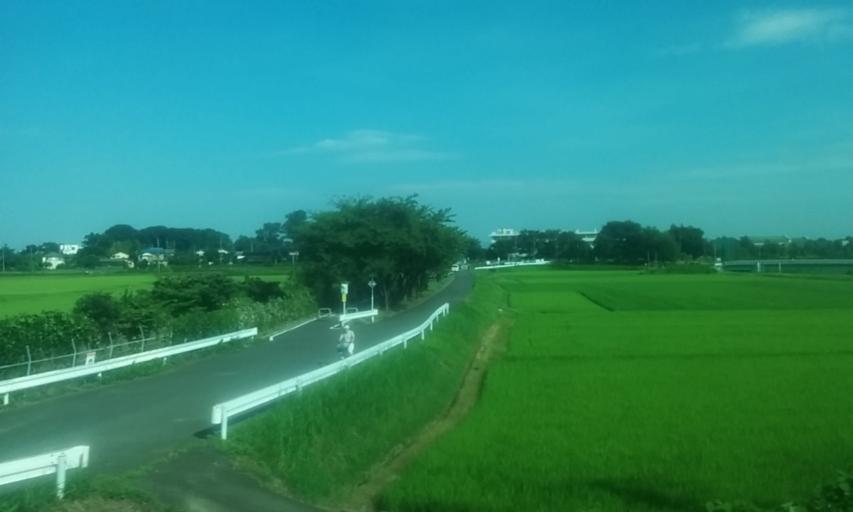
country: JP
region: Saitama
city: Hasuda
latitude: 35.9651
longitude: 139.6436
